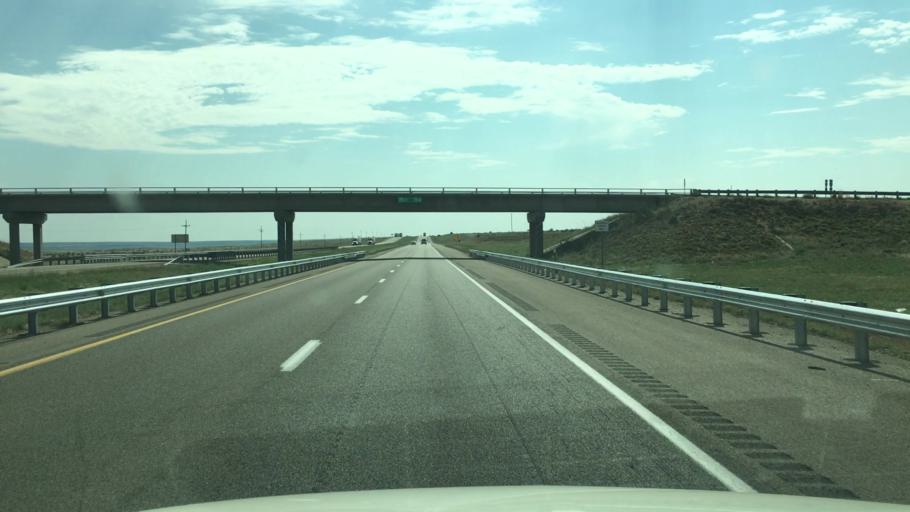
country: US
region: New Mexico
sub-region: Guadalupe County
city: Santa Rosa
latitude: 34.9801
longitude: -105.0674
